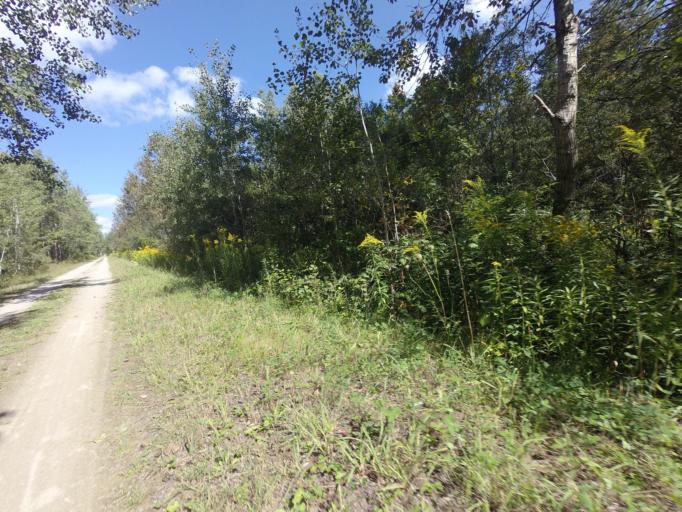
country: CA
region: Ontario
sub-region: Wellington County
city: Guelph
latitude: 43.7541
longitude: -80.3210
